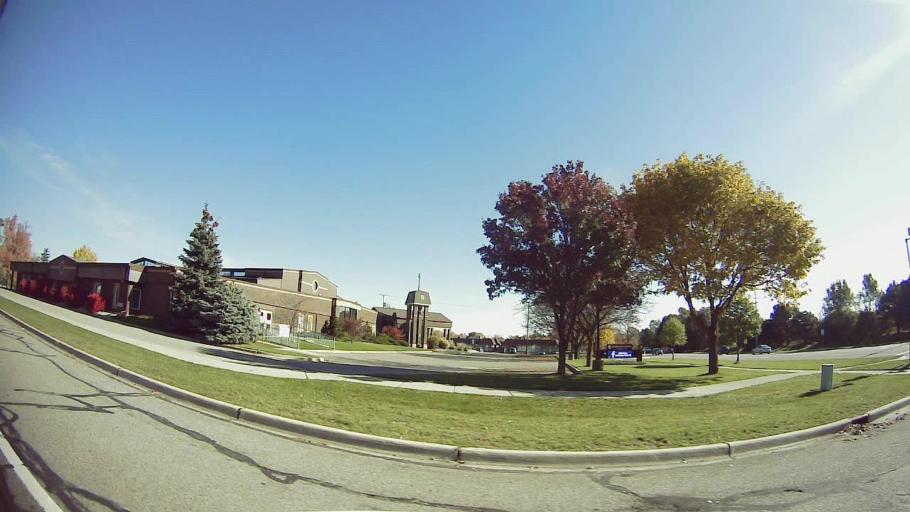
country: US
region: Michigan
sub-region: Oakland County
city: Farmington Hills
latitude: 42.5133
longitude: -83.3789
